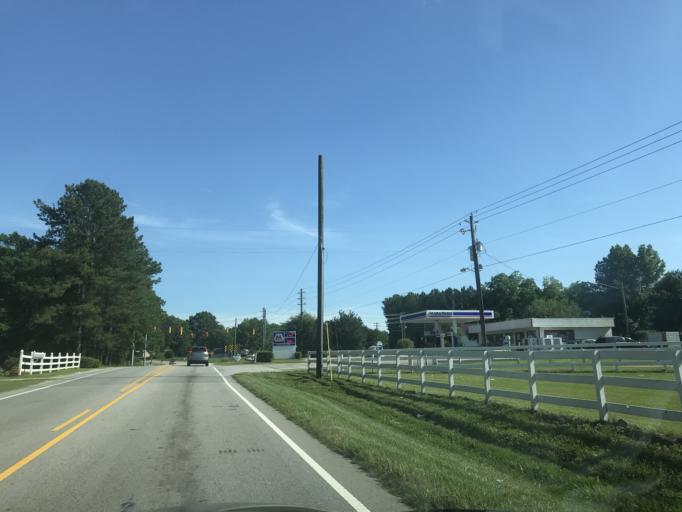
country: US
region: North Carolina
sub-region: Wake County
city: Garner
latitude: 35.6716
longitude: -78.5756
